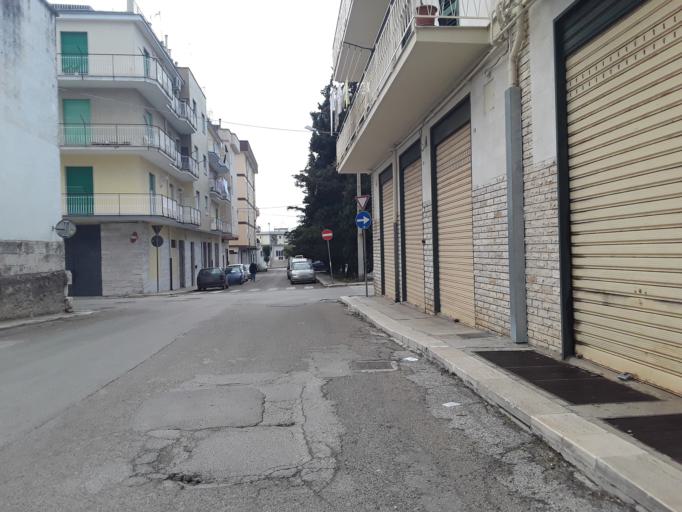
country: IT
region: Apulia
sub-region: Provincia di Bari
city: Ruvo di Puglia
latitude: 41.1202
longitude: 16.4813
